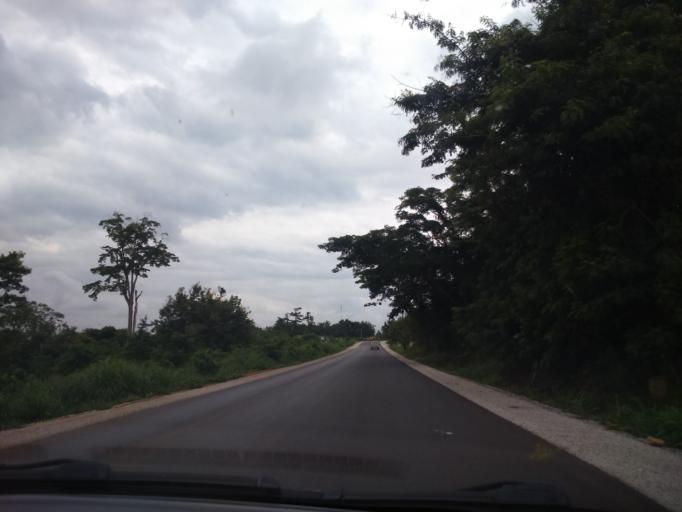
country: CI
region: Lagunes
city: Akoupe
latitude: 6.3349
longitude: -3.8492
